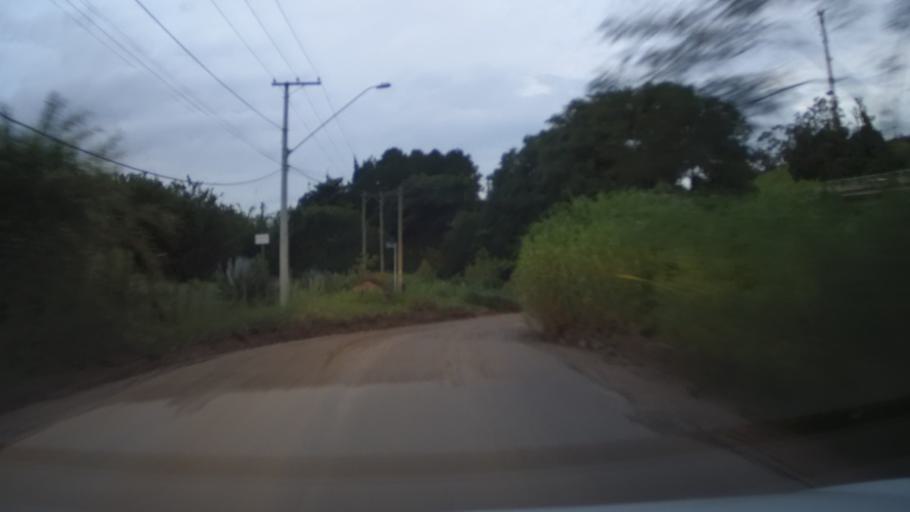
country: BR
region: Sao Paulo
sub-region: Vinhedo
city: Vinhedo
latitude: -23.0677
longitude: -47.0326
